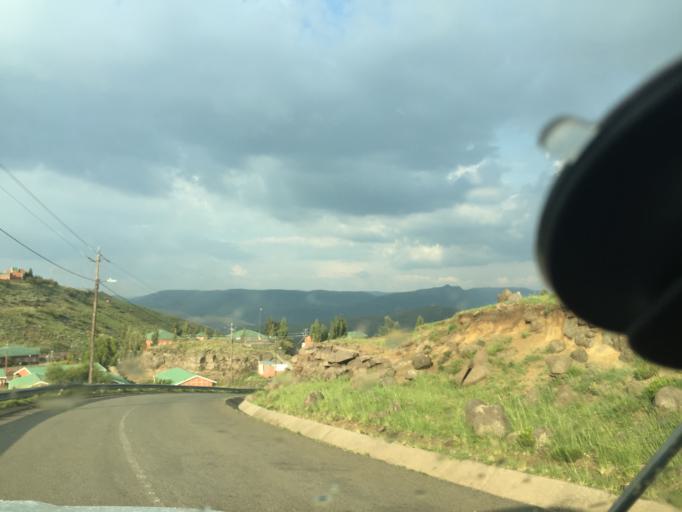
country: LS
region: Maseru
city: Nako
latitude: -29.4791
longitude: 28.0581
